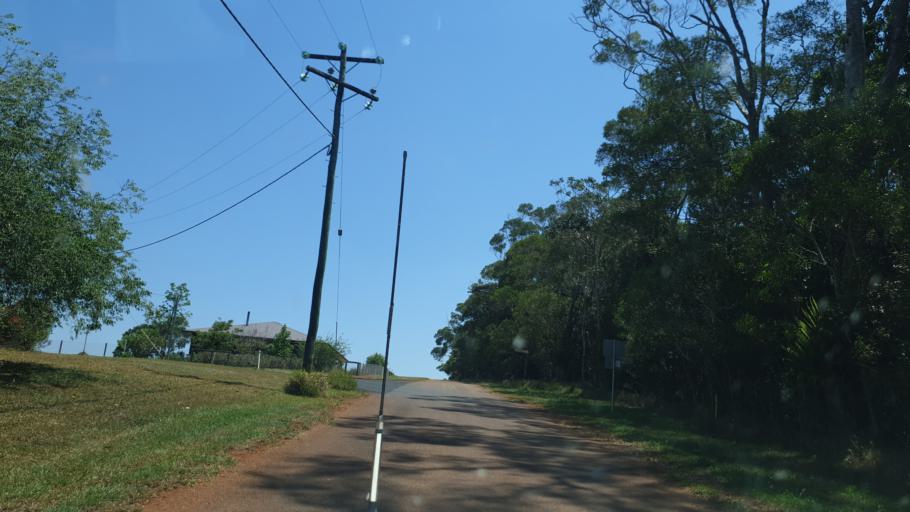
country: AU
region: Queensland
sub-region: Tablelands
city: Atherton
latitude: -17.3431
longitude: 145.6239
